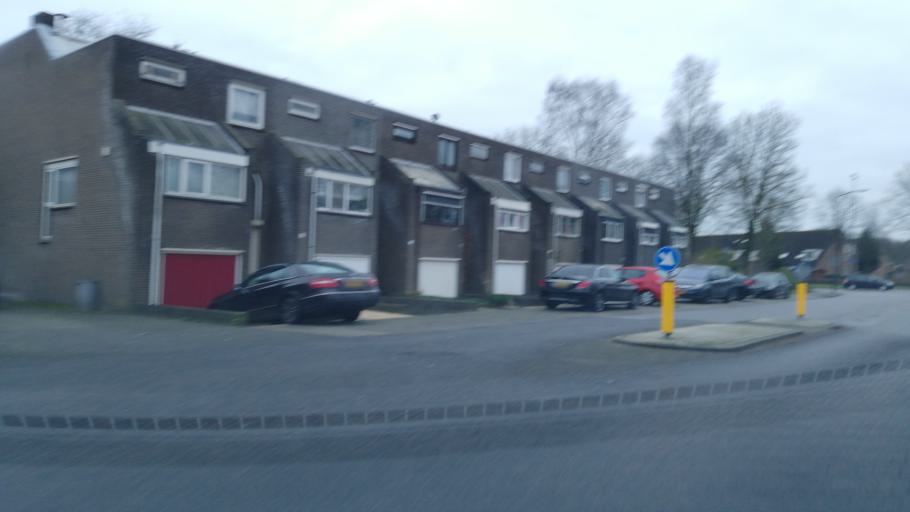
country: NL
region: Gelderland
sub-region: Gemeente Apeldoorn
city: Apeldoorn
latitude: 52.2032
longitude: 5.9960
